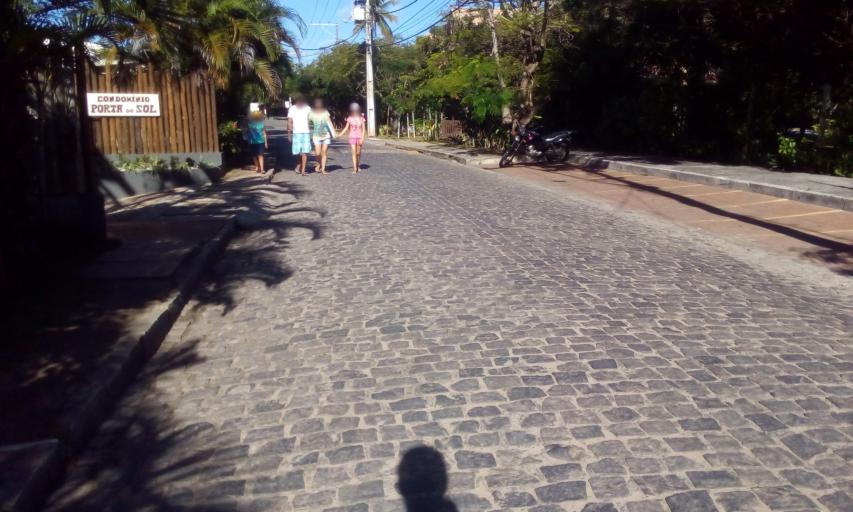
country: BR
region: Bahia
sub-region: Mata De Sao Joao
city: Mata de Sao Joao
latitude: -12.5778
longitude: -38.0086
